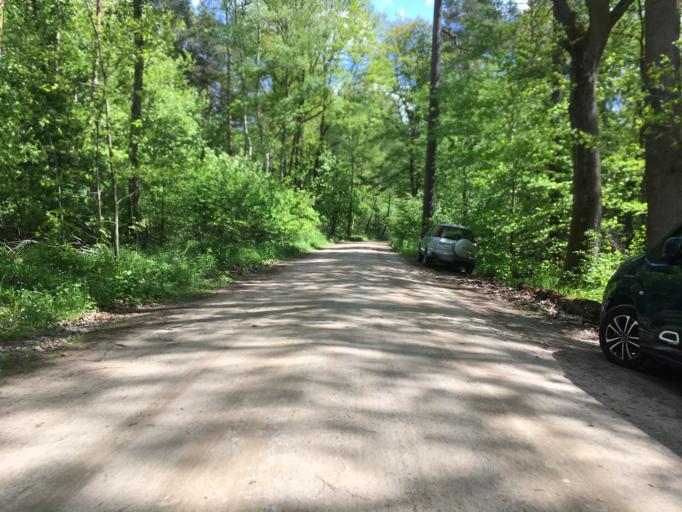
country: DE
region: Brandenburg
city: Friedrichswalde
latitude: 53.0064
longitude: 13.6320
